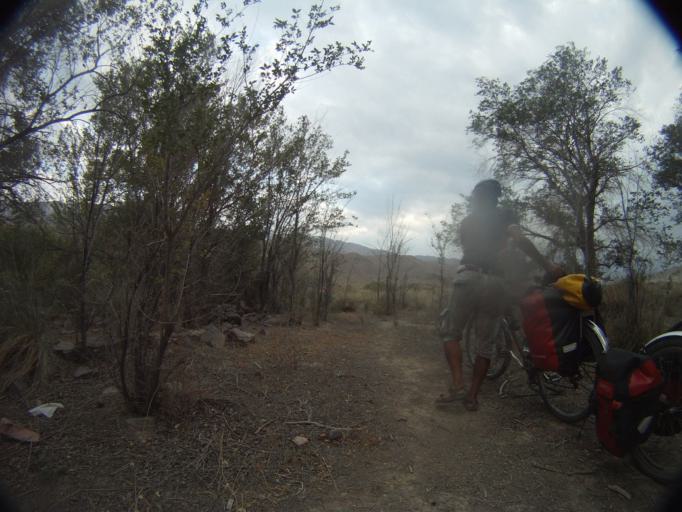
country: KG
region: Ysyk-Koel
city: Balykchy
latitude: 42.4676
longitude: 75.9515
